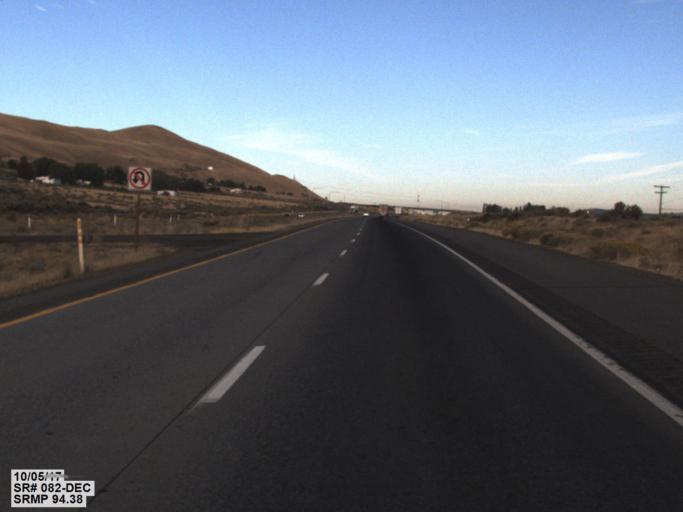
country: US
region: Washington
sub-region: Benton County
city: Benton City
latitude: 46.2610
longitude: -119.5194
